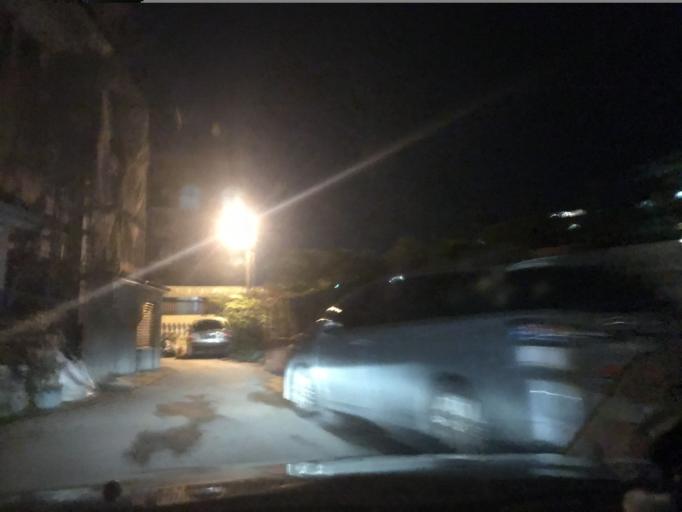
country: TW
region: Taiwan
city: Taoyuan City
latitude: 24.9435
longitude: 121.2463
